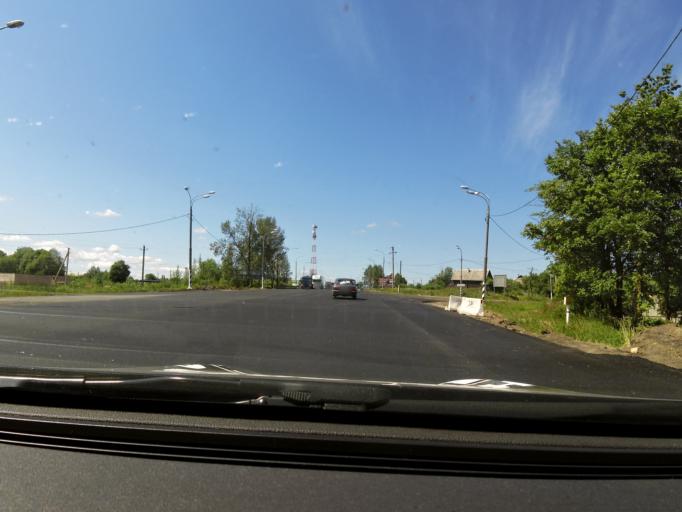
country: RU
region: Novgorod
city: Valday
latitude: 57.9517
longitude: 33.2915
